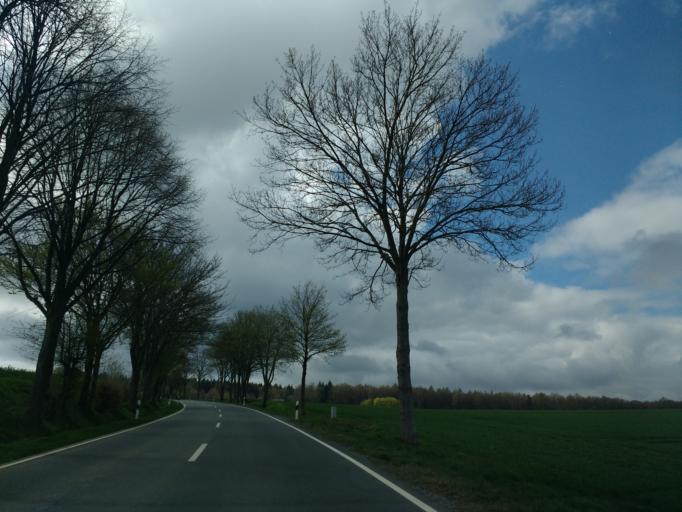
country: DE
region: North Rhine-Westphalia
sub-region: Regierungsbezirk Detmold
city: Wunnenberg
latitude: 51.5059
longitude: 8.7396
